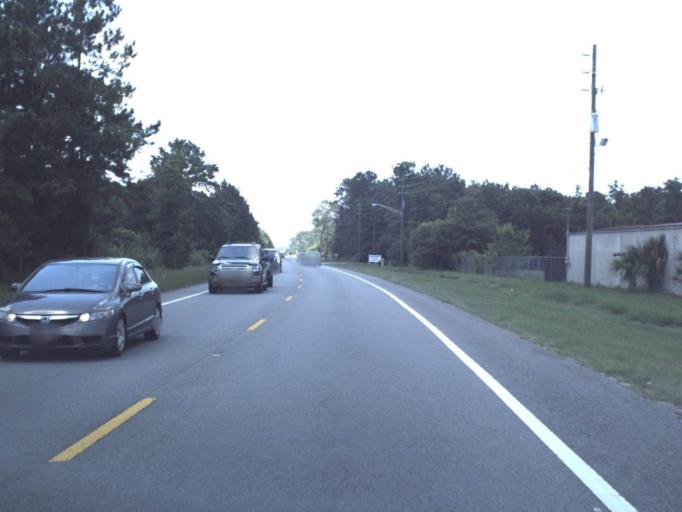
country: US
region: Florida
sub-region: Nassau County
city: Yulee
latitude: 30.4965
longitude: -81.6231
